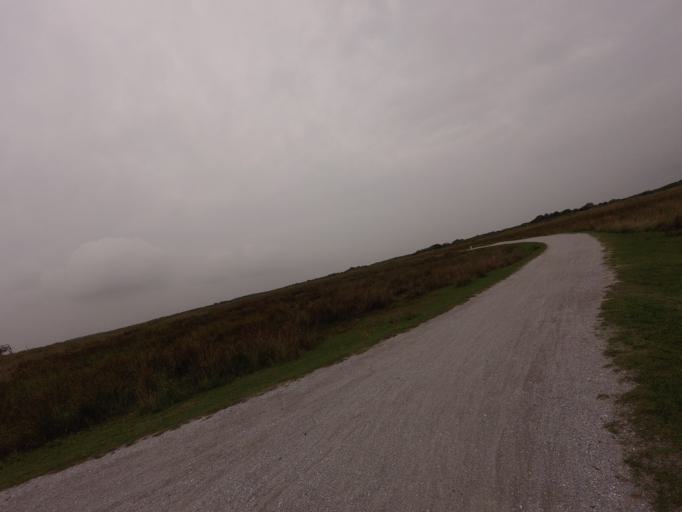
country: NL
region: Friesland
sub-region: Gemeente Schiermonnikoog
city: Schiermonnikoog
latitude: 53.4874
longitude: 6.2093
